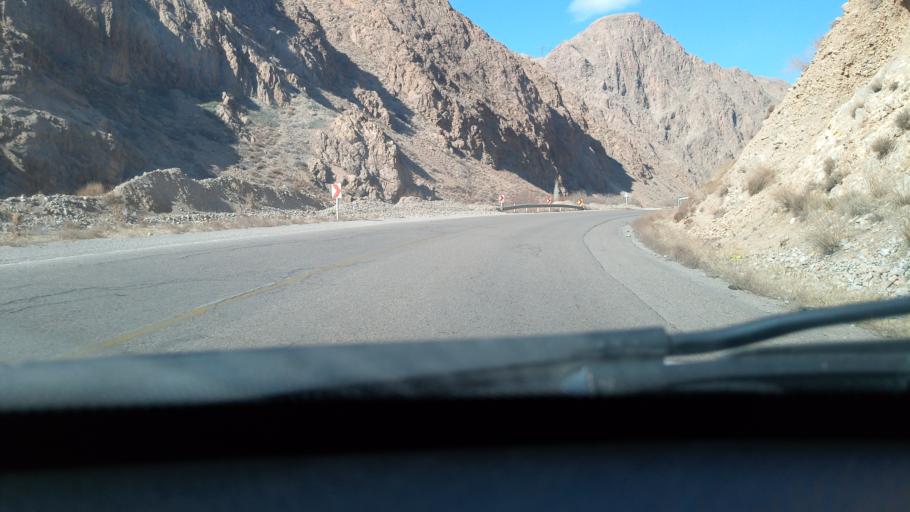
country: IR
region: Khorasan-e Shomali
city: Esfarayen
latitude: 37.1716
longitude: 57.4227
